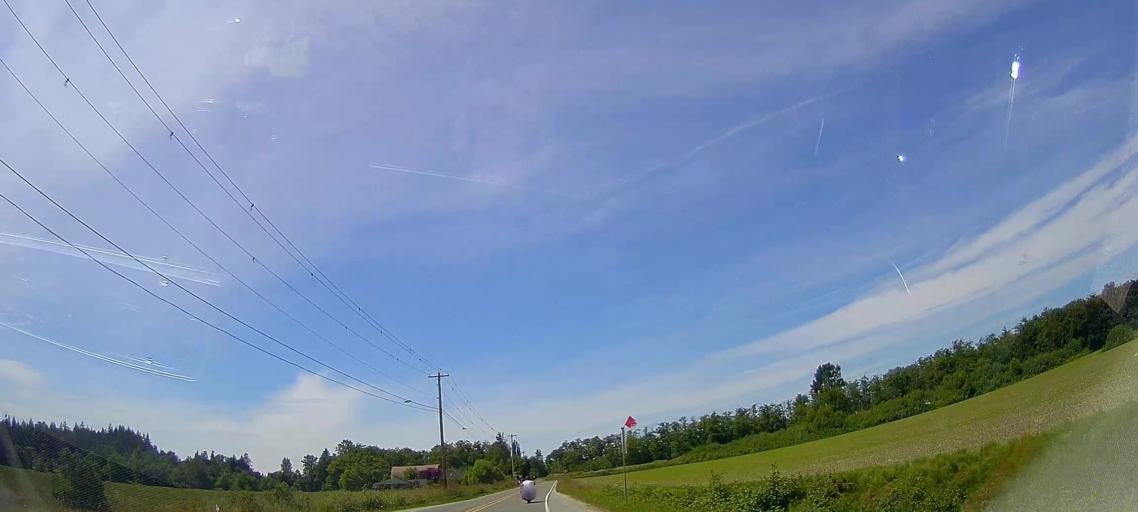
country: US
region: Washington
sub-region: Snohomish County
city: Smokey Point
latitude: 48.1891
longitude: -122.2278
